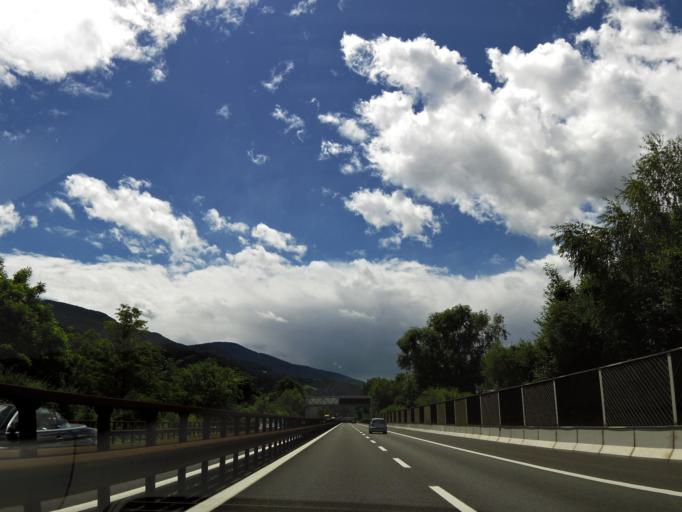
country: IT
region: Trentino-Alto Adige
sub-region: Bolzano
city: Bressanone
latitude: 46.6966
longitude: 11.6429
